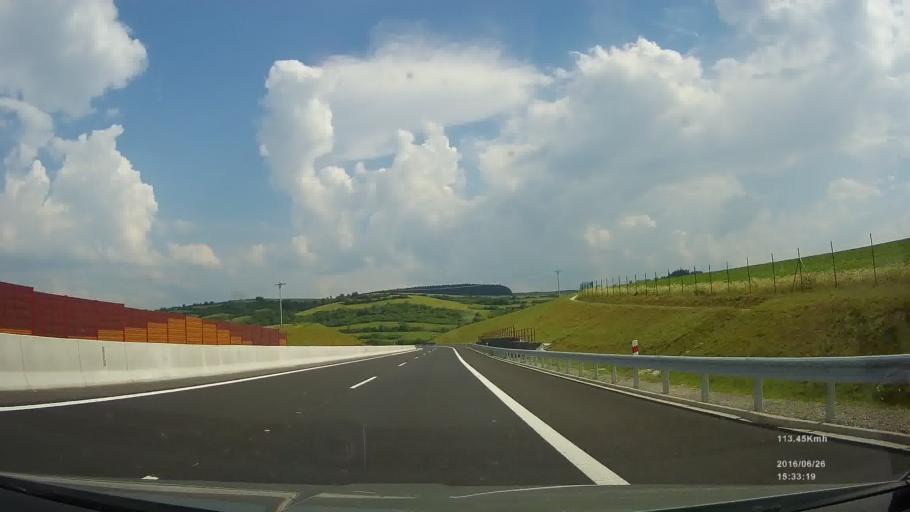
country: SK
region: Presovsky
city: Sabinov
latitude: 49.0035
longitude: 21.0563
